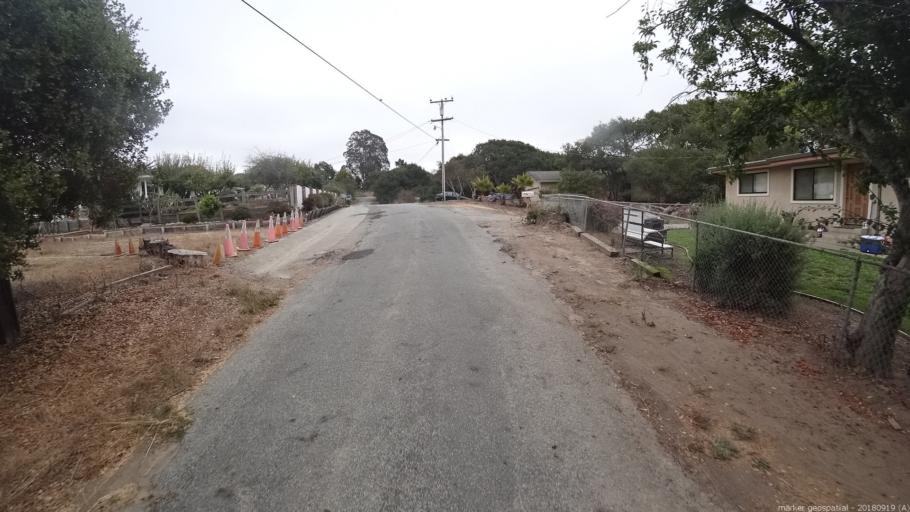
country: US
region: California
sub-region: Monterey County
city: Elkhorn
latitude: 36.8039
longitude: -121.7283
